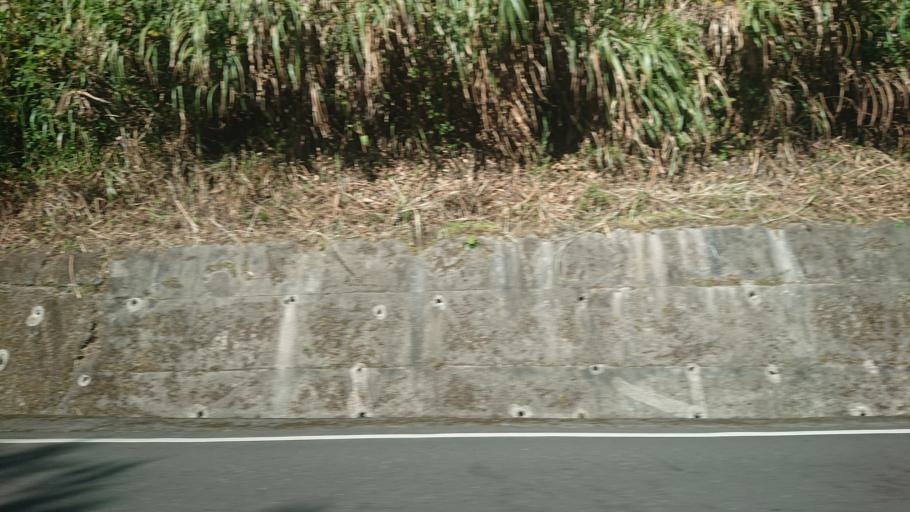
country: TW
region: Taiwan
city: Lugu
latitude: 23.4667
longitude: 120.7303
